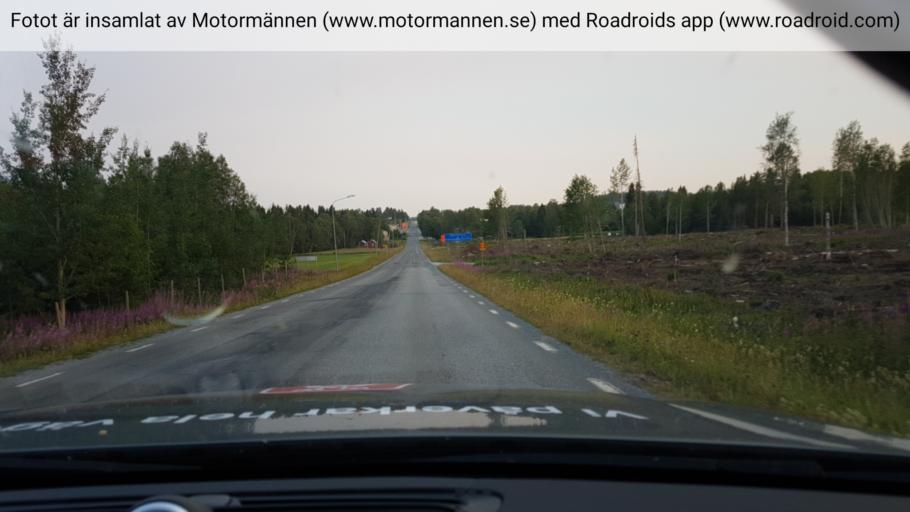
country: SE
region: Jaemtland
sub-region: Bergs Kommun
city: Hoverberg
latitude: 63.0286
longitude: 14.3402
